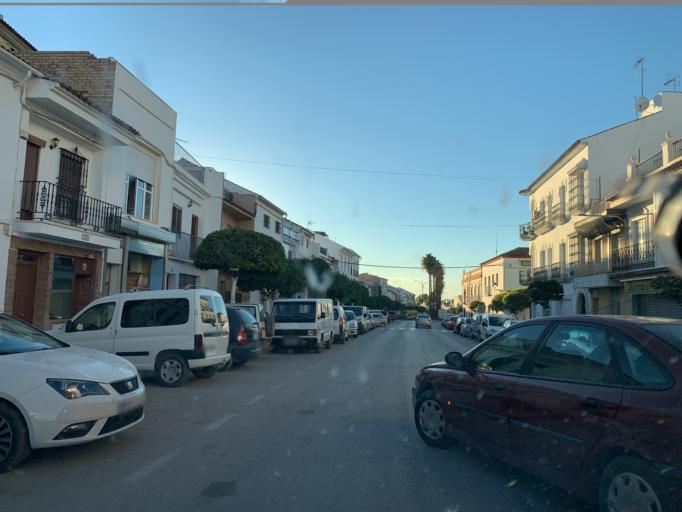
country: ES
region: Andalusia
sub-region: Provincia de Sevilla
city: Pedrera
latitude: 37.2227
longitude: -4.8957
